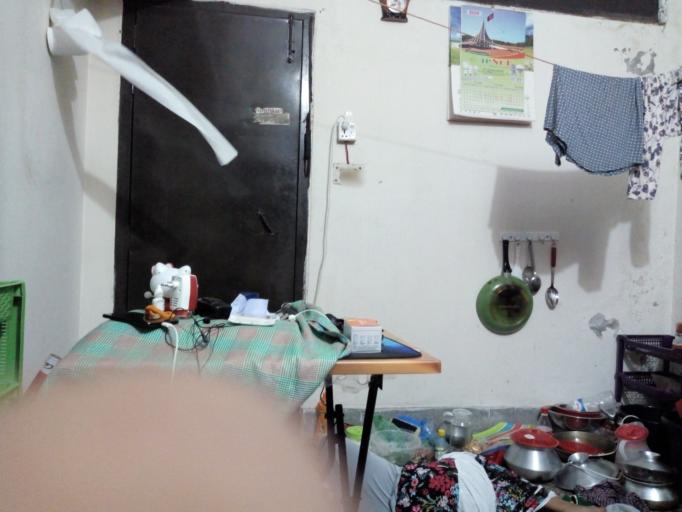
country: BD
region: Dhaka
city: Azimpur
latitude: 23.8043
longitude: 90.3663
